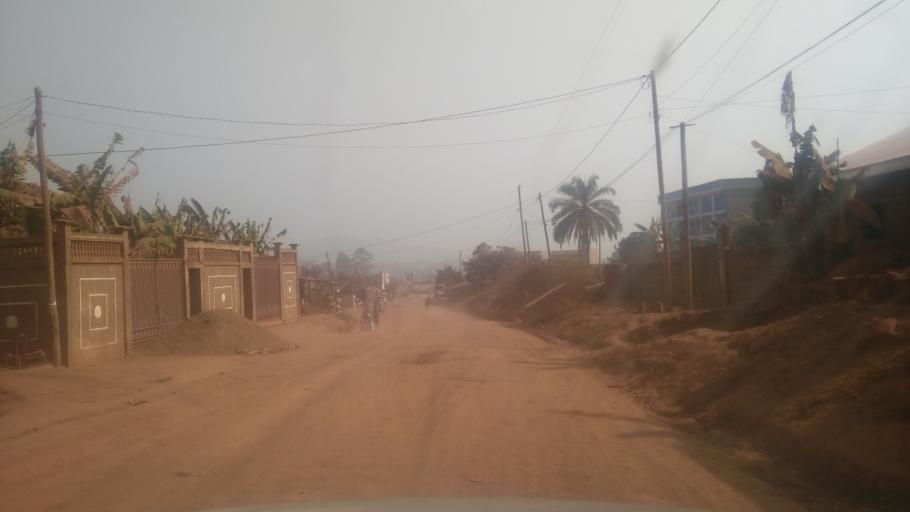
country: CM
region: West
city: Bafoussam
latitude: 5.5083
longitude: 10.4024
